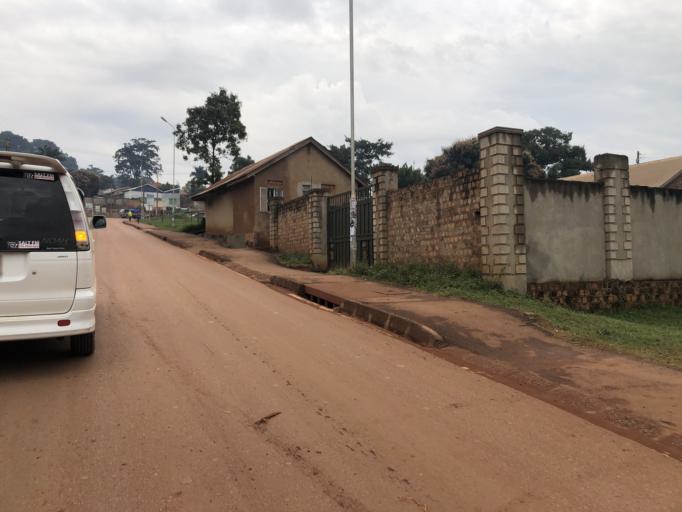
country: UG
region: Central Region
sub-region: Kampala District
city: Kampala
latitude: 0.2799
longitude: 32.6001
